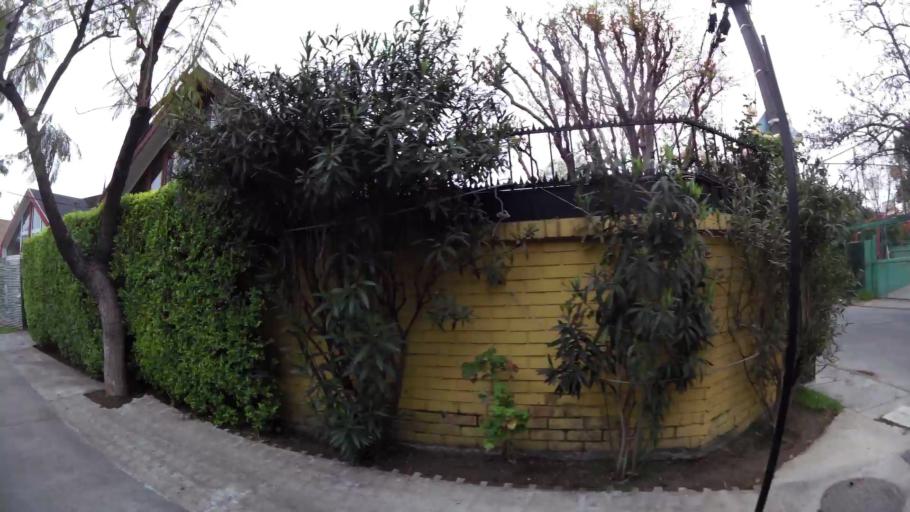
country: CL
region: Santiago Metropolitan
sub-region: Provincia de Santiago
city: Villa Presidente Frei, Nunoa, Santiago, Chile
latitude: -33.3876
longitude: -70.5575
